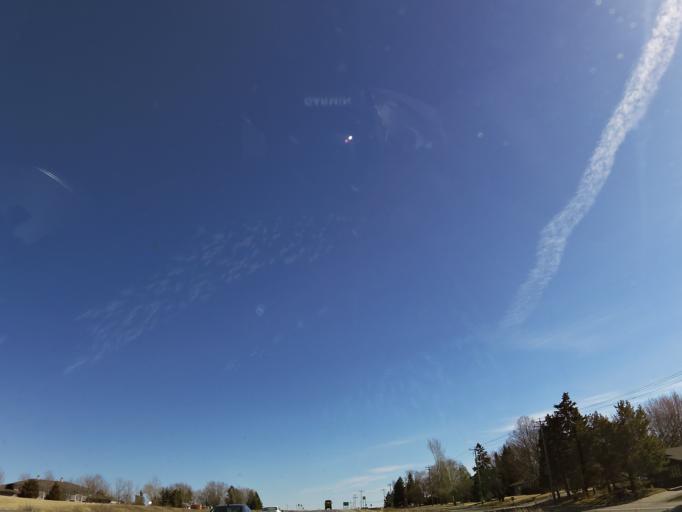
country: US
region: Minnesota
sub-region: Hennepin County
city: Wayzata
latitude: 45.0371
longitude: -93.5151
